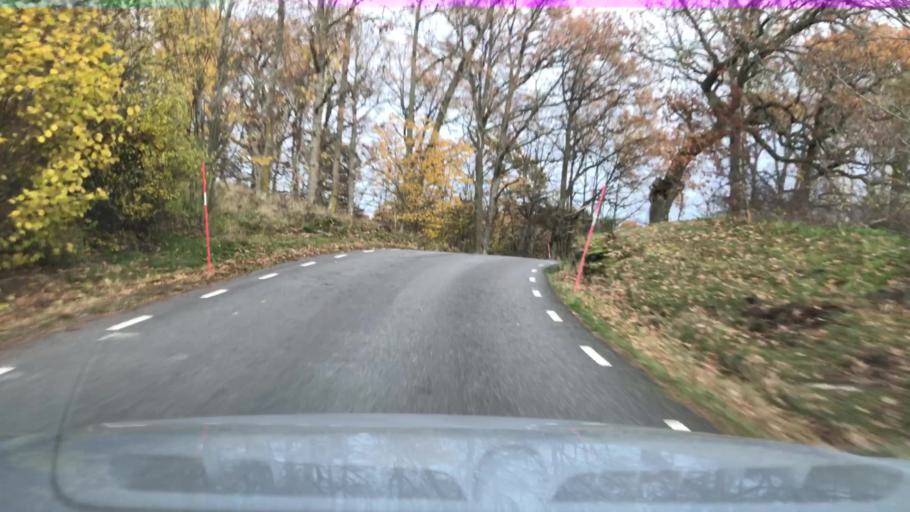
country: SE
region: OEstergoetland
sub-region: Valdemarsviks Kommun
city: Valdemarsvik
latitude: 58.2856
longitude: 16.7570
